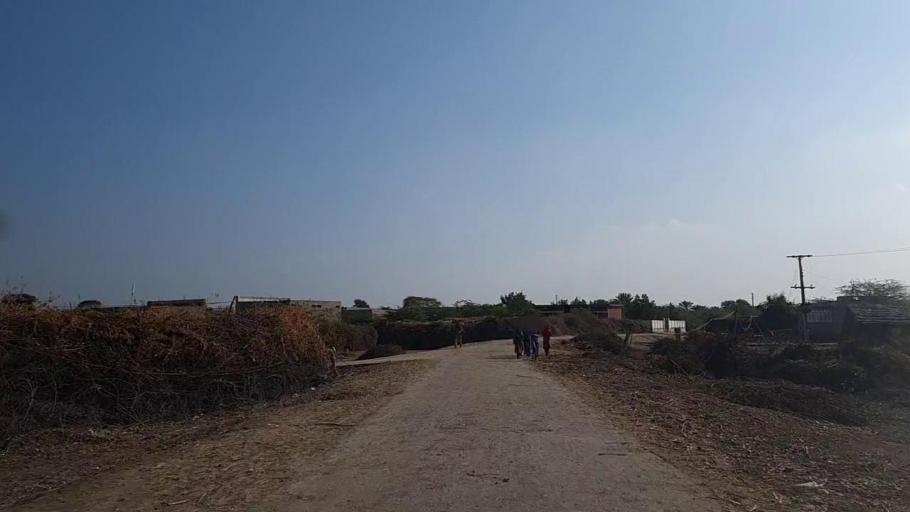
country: PK
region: Sindh
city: Jam Sahib
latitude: 26.2751
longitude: 68.5839
